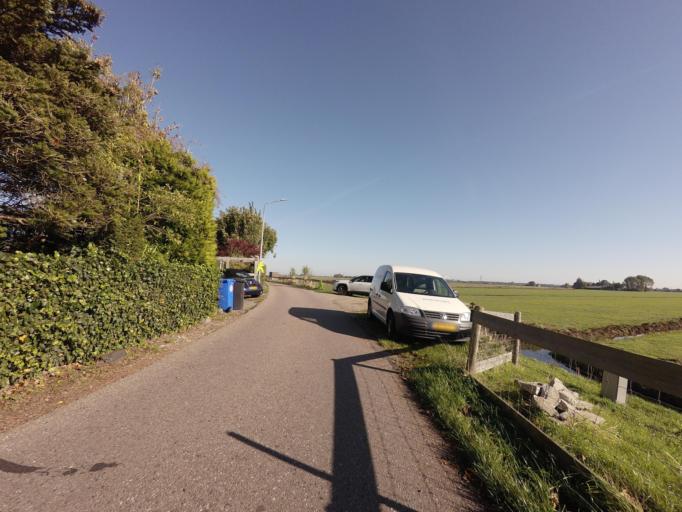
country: NL
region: North Holland
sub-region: Gemeente Weesp
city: Weesp
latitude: 52.3097
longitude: 5.0574
